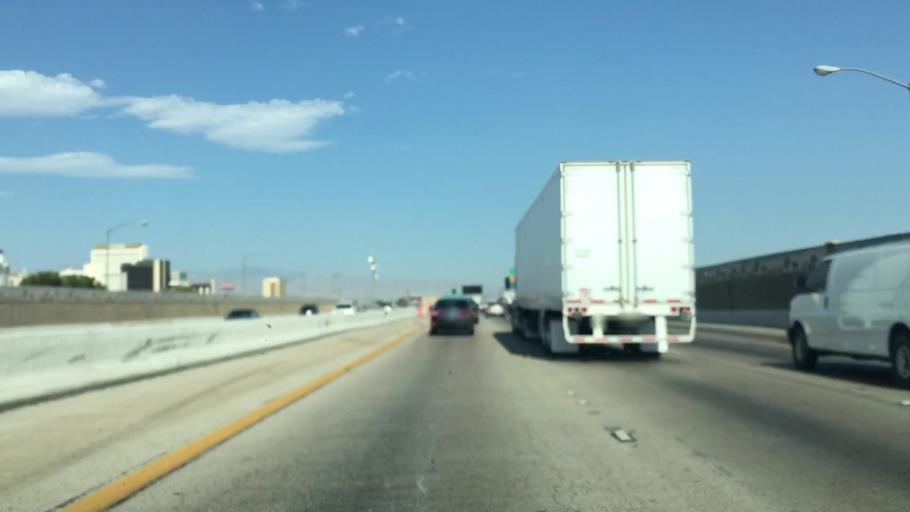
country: US
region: Nevada
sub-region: Clark County
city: Las Vegas
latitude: 36.1710
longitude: -115.1316
